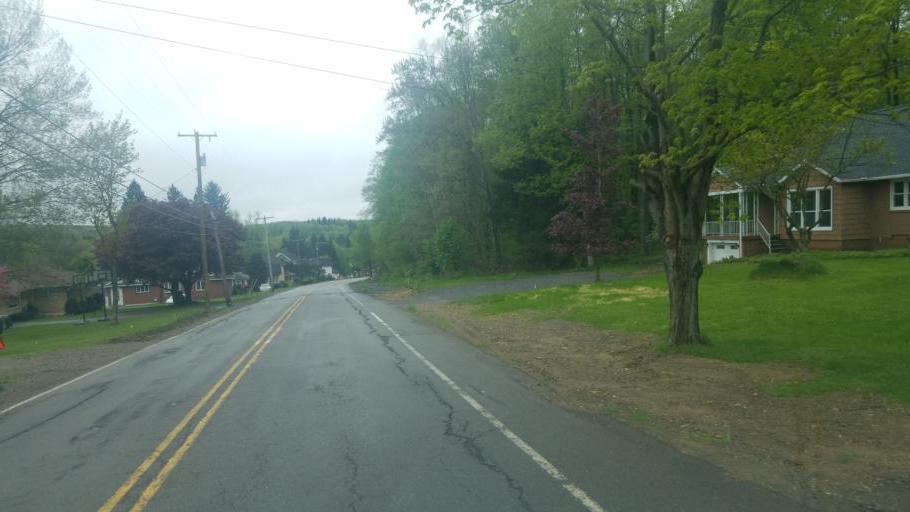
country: US
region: Pennsylvania
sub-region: McKean County
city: Kane
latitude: 41.6430
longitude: -78.8142
